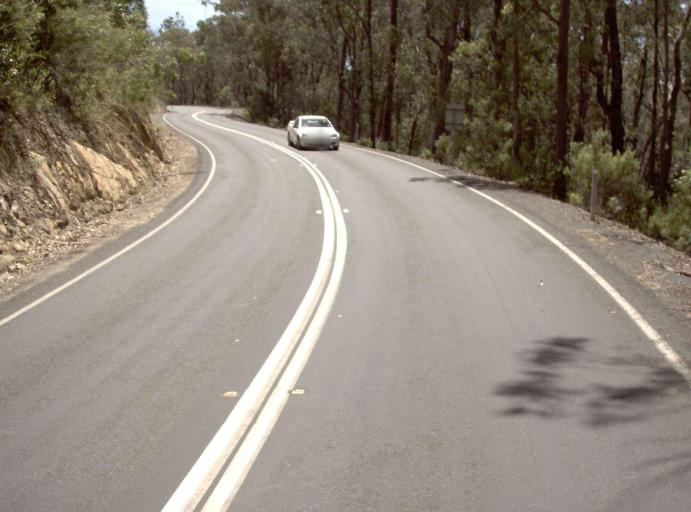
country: AU
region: Victoria
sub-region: East Gippsland
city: Lakes Entrance
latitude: -37.6227
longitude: 147.8825
